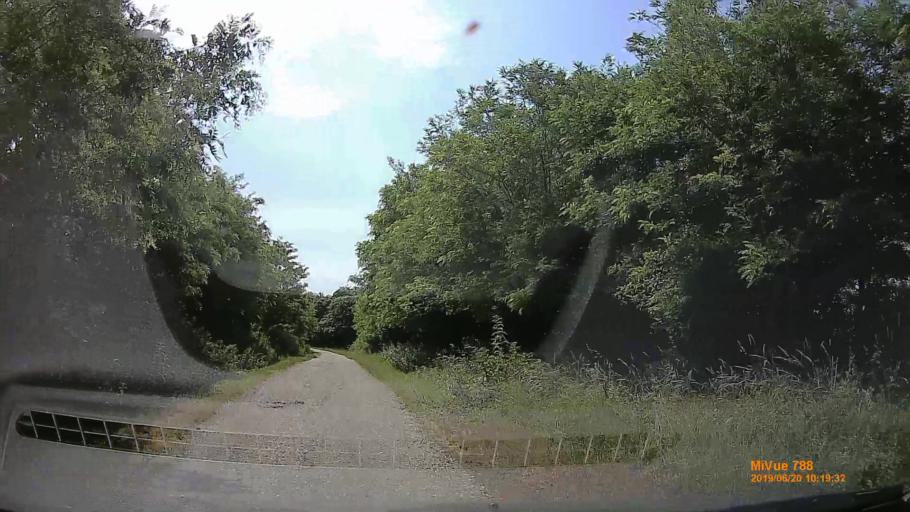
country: HU
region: Baranya
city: Mecseknadasd
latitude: 46.2109
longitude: 18.4617
